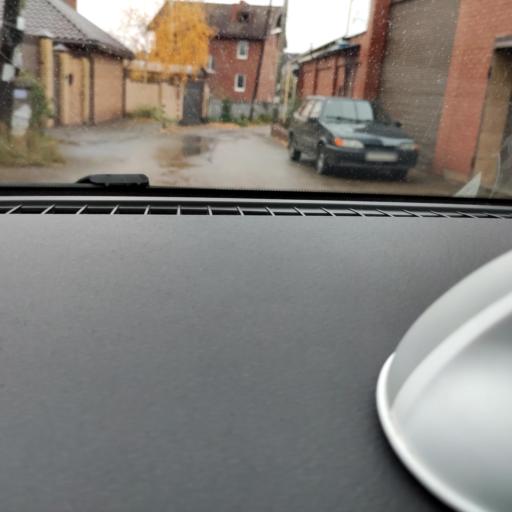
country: RU
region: Samara
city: Samara
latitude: 53.2701
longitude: 50.2061
